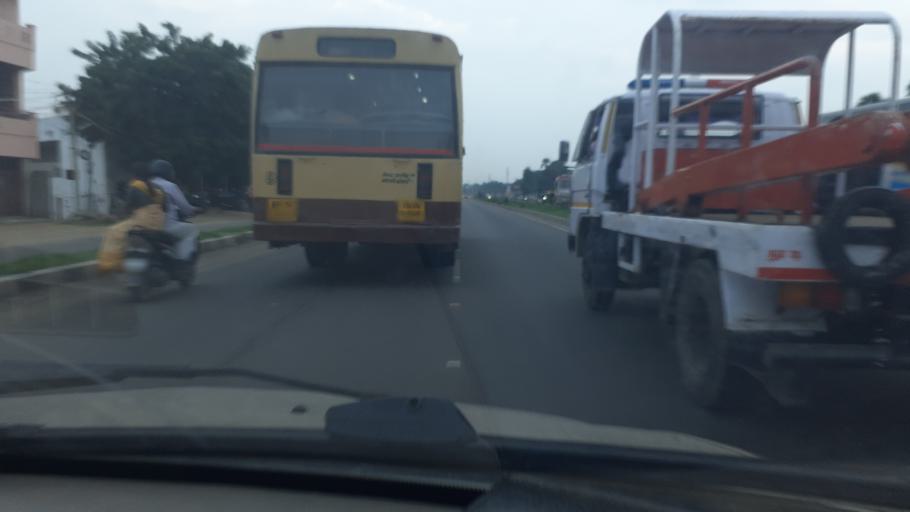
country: IN
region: Tamil Nadu
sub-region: Thoothukkudi
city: Korampallam
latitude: 8.7788
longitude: 78.0942
